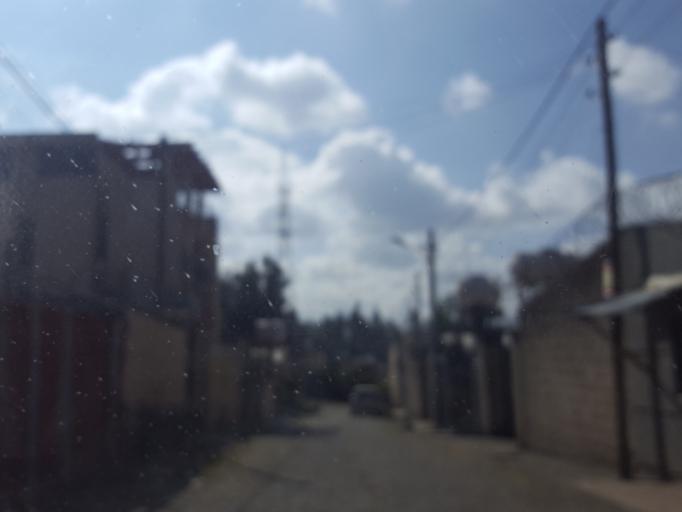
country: ET
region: Adis Abeba
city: Addis Ababa
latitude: 9.0688
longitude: 38.7197
